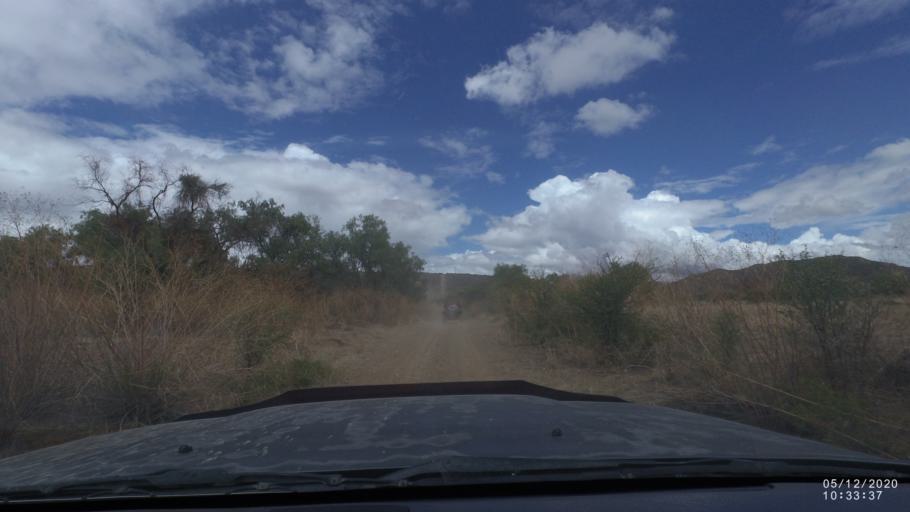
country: BO
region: Cochabamba
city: Sipe Sipe
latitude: -17.5458
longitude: -66.2738
